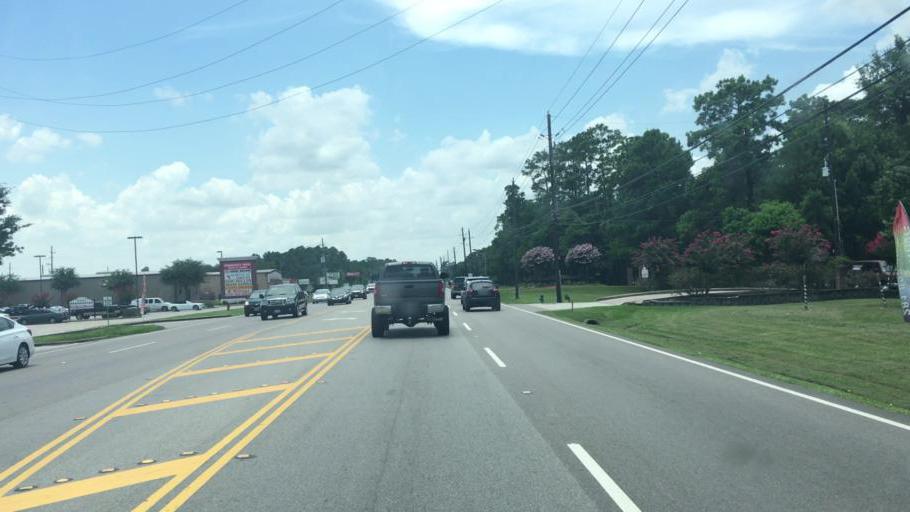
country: US
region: Texas
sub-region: Harris County
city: Atascocita
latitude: 29.9883
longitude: -95.1933
